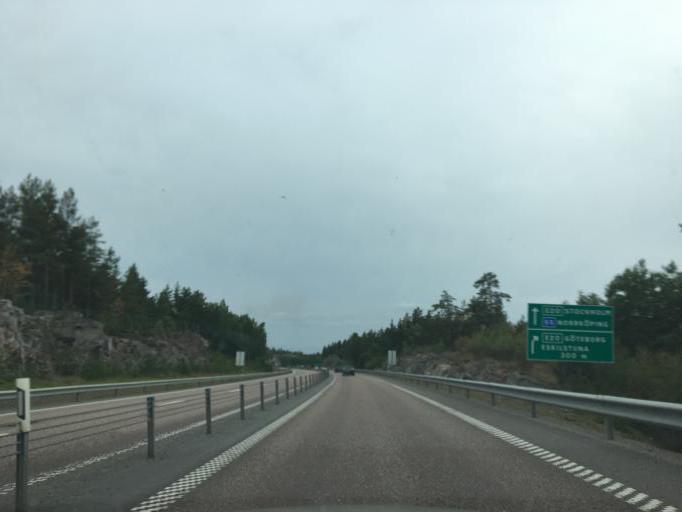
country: SE
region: Soedermanland
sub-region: Strangnas Kommun
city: Strangnas
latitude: 59.3728
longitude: 16.9621
